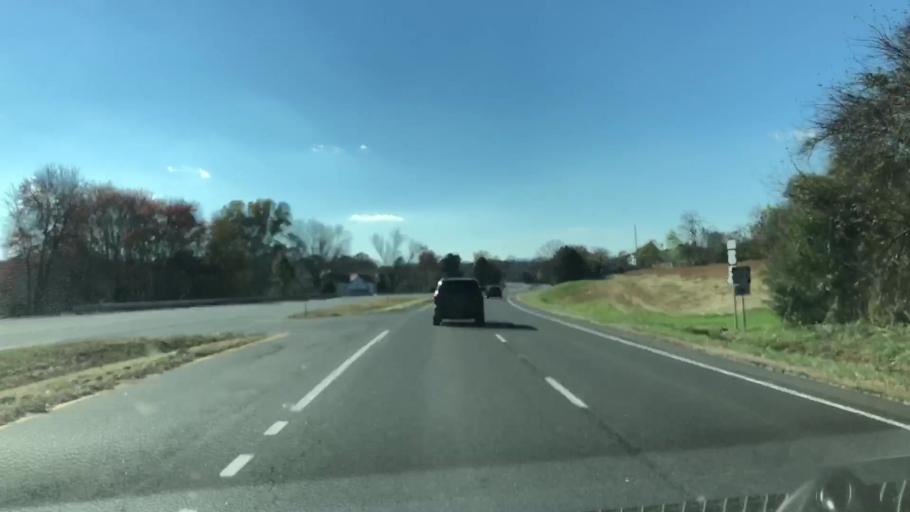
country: US
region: Virginia
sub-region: Madison County
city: Brightwood
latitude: 38.4210
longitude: -78.1915
